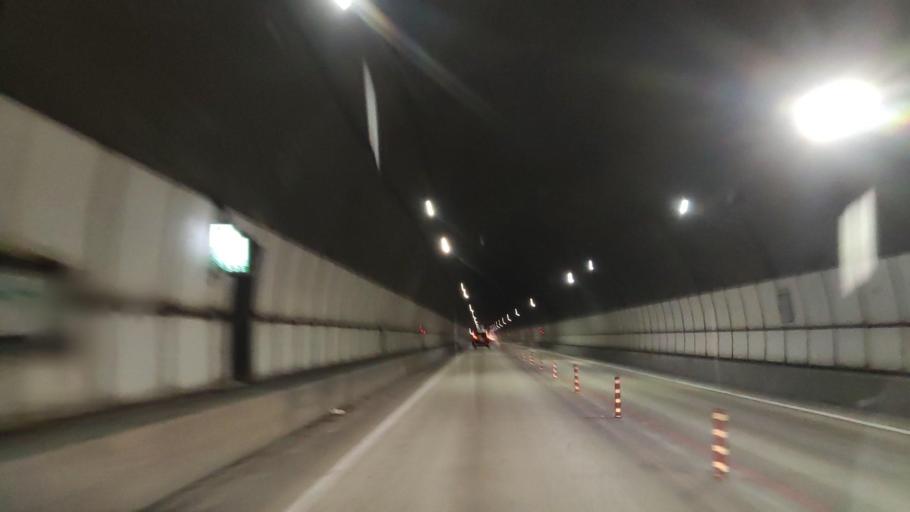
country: JP
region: Yamagata
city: Shinjo
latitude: 38.6875
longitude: 140.3140
